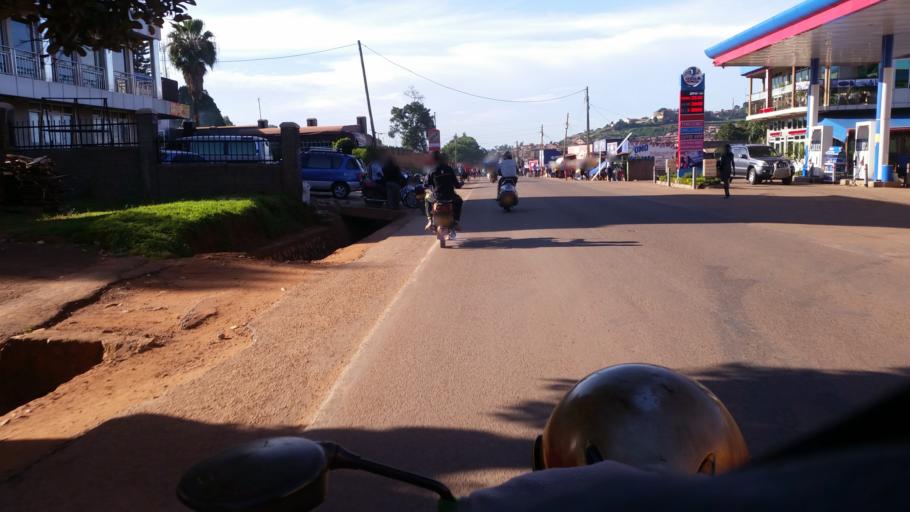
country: UG
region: Central Region
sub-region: Wakiso District
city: Kireka
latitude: 0.3236
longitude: 32.6367
